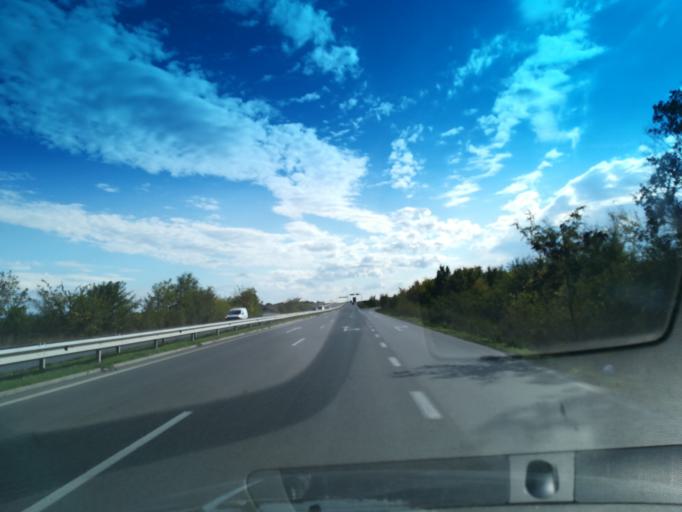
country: BG
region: Stara Zagora
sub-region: Obshtina Stara Zagora
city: Stara Zagora
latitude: 42.3440
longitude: 25.6606
